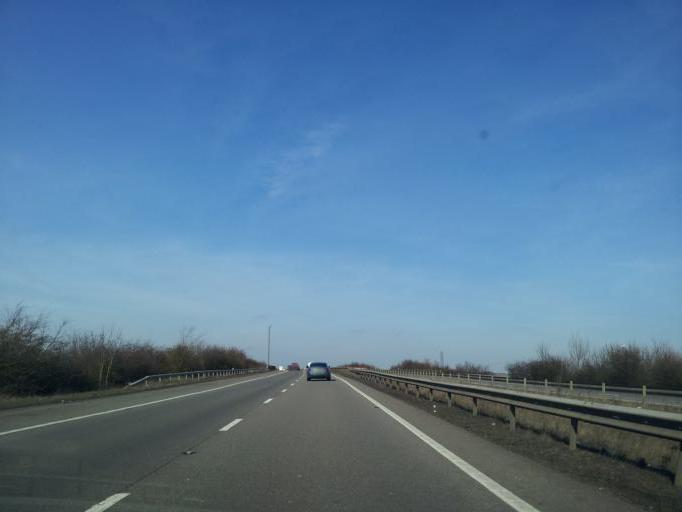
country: GB
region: England
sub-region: Cambridgeshire
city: Brampton
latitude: 52.3307
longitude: -0.2480
